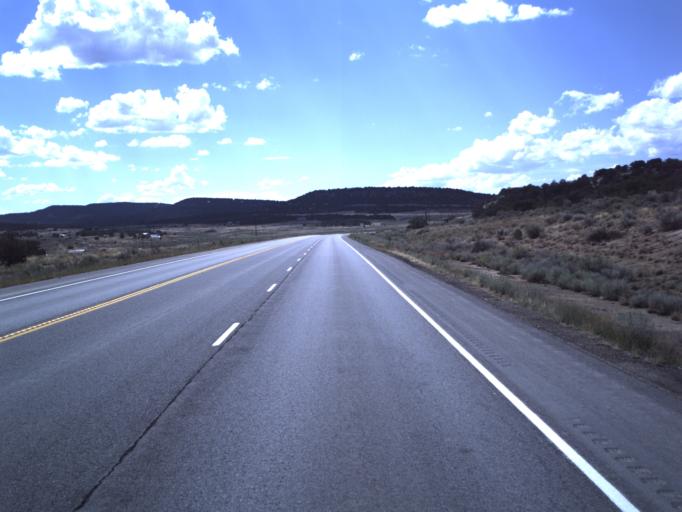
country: US
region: Utah
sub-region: Duchesne County
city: Duchesne
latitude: 40.1721
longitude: -110.5808
